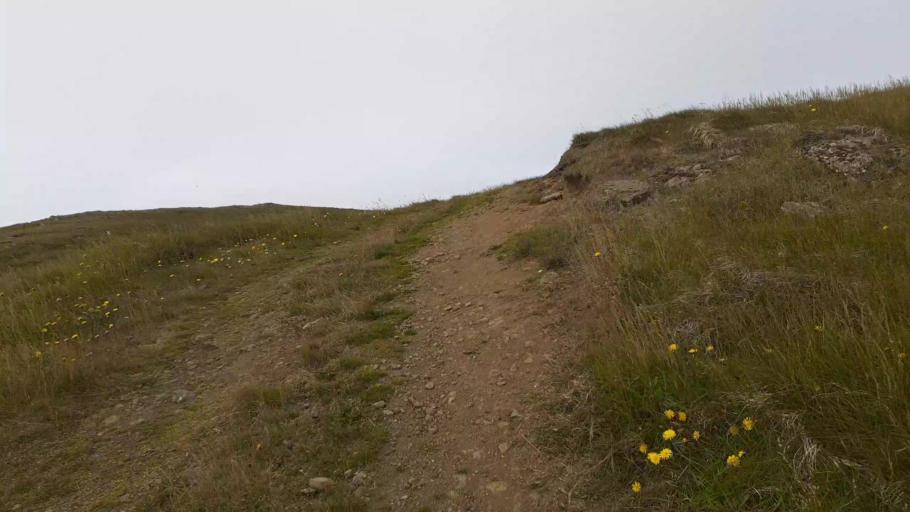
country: IS
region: Northeast
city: Dalvik
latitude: 66.5346
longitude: -17.9832
